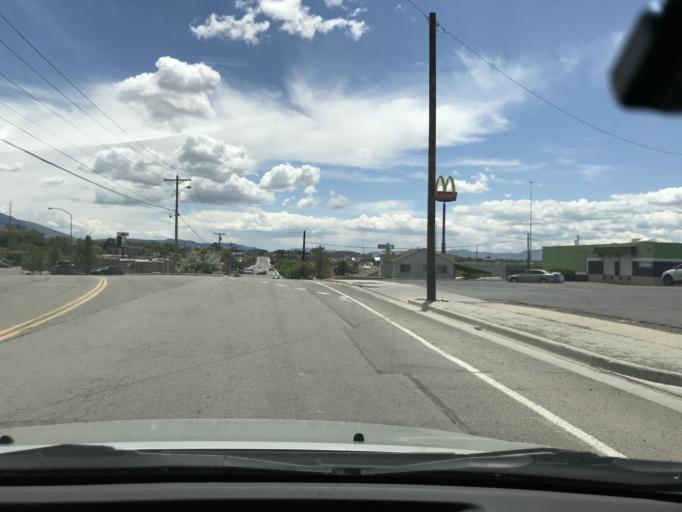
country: US
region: Utah
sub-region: Salt Lake County
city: Centerfield
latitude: 40.6766
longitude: -111.8998
